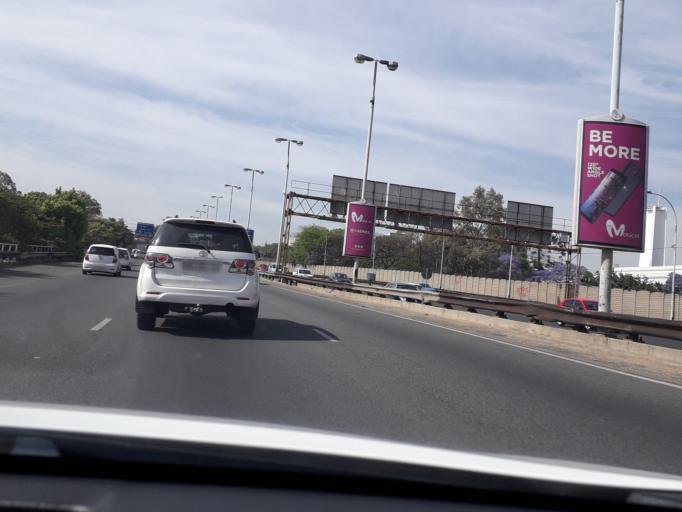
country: ZA
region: Gauteng
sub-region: City of Johannesburg Metropolitan Municipality
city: Johannesburg
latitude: -26.1871
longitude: 28.0276
